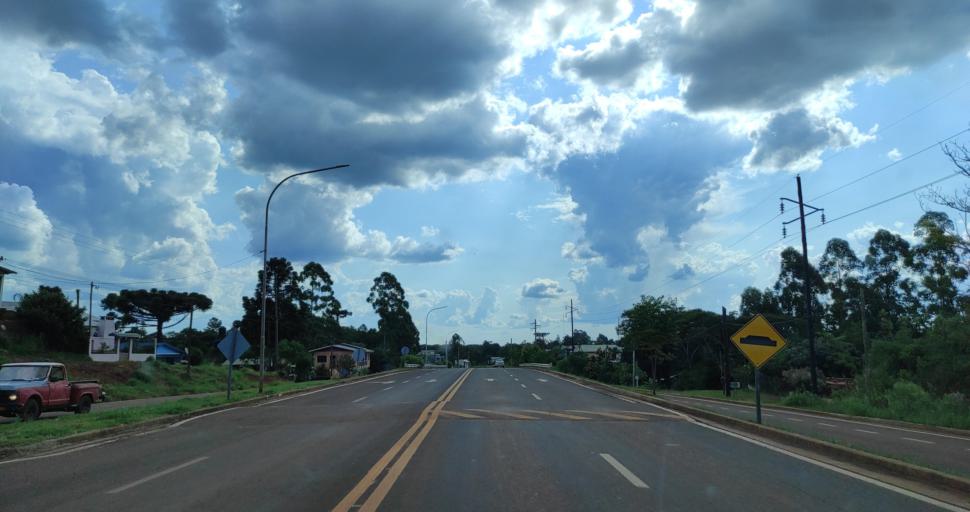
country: AR
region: Misiones
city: Bernardo de Irigoyen
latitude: -26.2944
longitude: -53.7456
